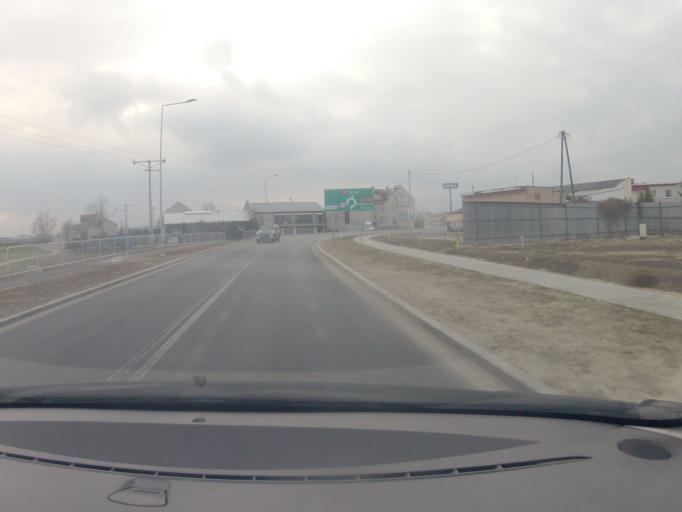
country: PL
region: Subcarpathian Voivodeship
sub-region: Powiat jasielski
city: Jaslo
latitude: 49.7515
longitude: 21.4757
